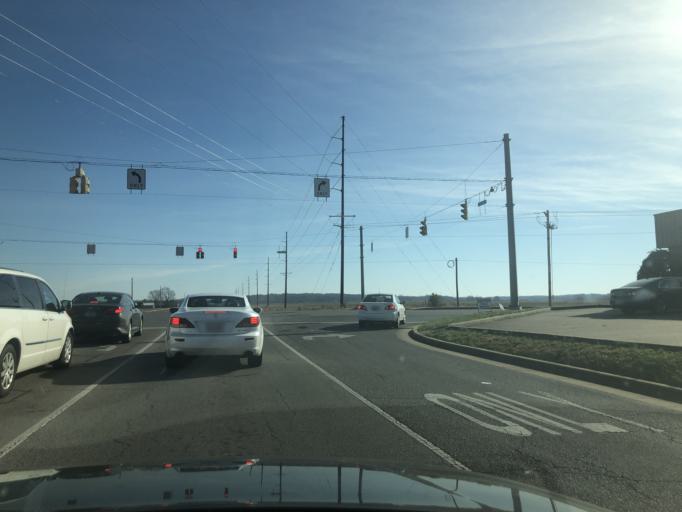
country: US
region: Indiana
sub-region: Warrick County
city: Newburgh
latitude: 37.9913
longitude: -87.4415
